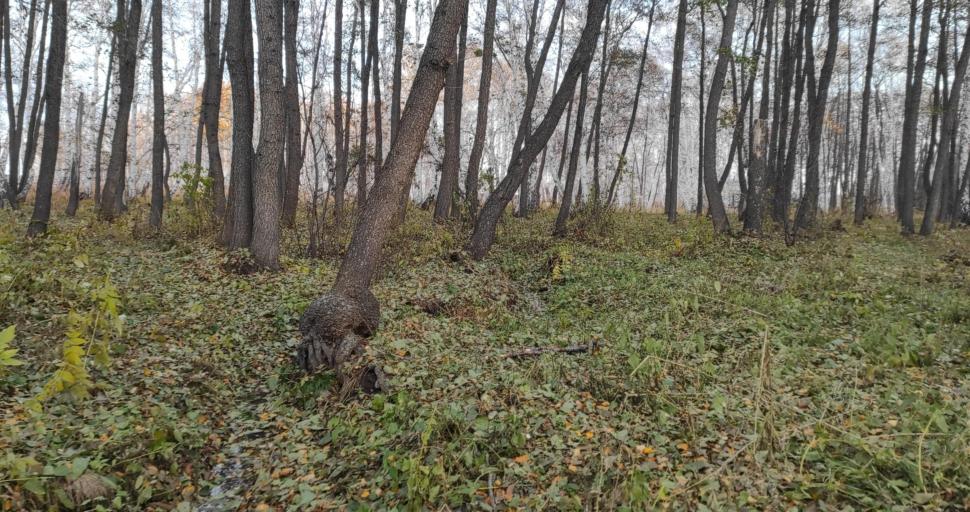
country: RU
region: Bashkortostan
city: Sibay
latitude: 52.6548
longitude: 58.5704
